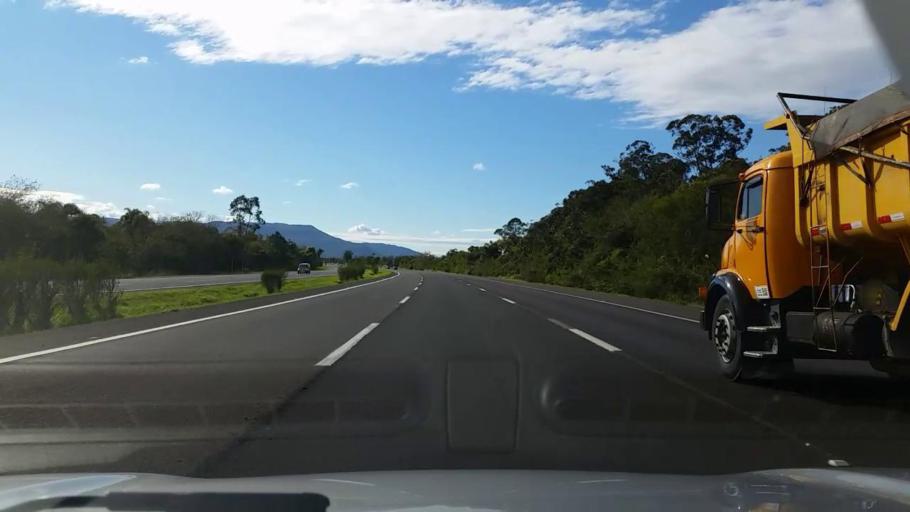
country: BR
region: Rio Grande do Sul
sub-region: Osorio
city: Osorio
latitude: -29.8901
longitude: -50.4668
